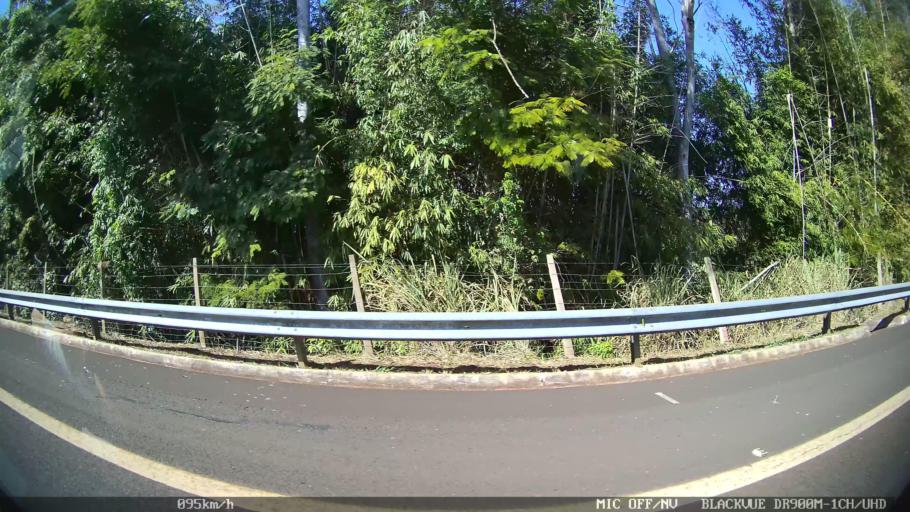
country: BR
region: Sao Paulo
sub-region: Batatais
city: Batatais
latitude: -20.7318
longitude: -47.5246
